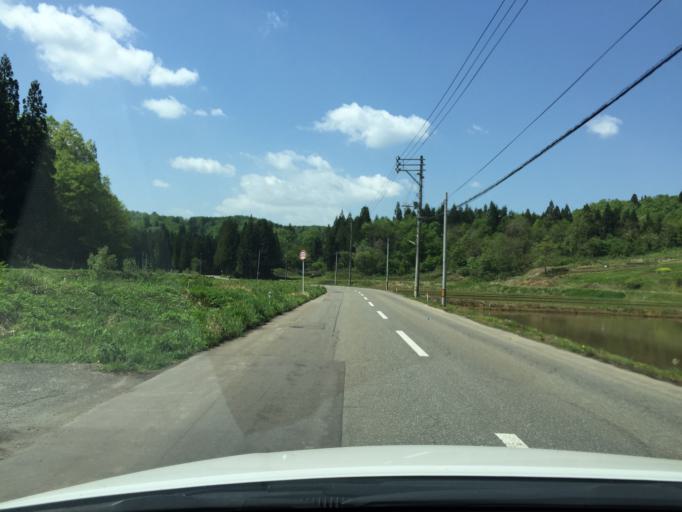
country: JP
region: Niigata
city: Tochio-honcho
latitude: 37.5075
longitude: 139.0725
